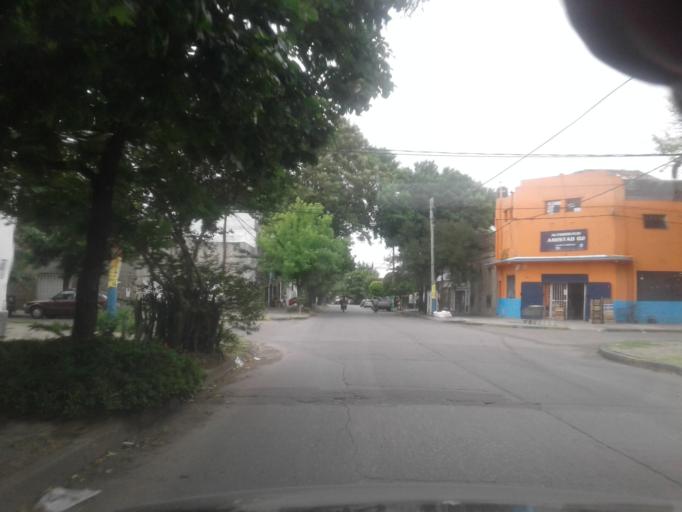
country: AR
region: Santa Fe
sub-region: Departamento de Rosario
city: Rosario
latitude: -32.9347
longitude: -60.6834
